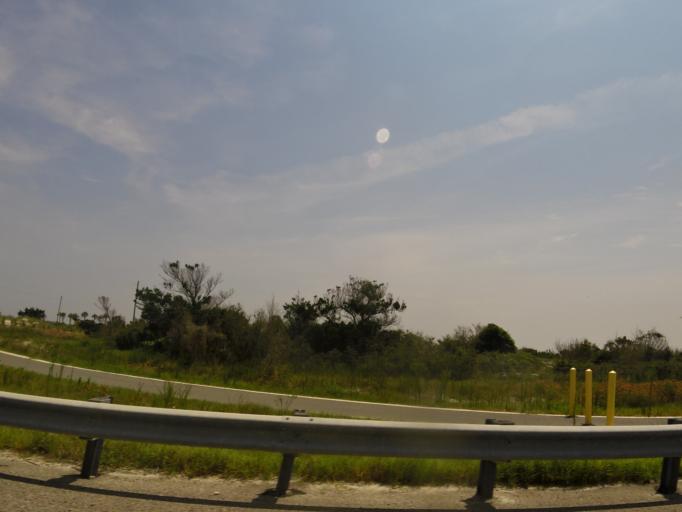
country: US
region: Florida
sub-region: Duval County
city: Atlantic Beach
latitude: 30.4290
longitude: -81.4115
